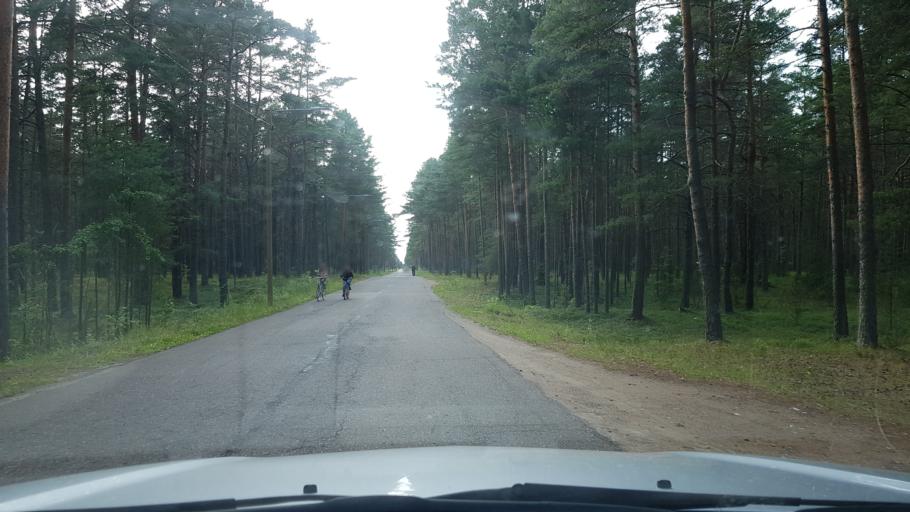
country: EE
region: Ida-Virumaa
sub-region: Narva-Joesuu linn
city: Narva-Joesuu
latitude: 59.4498
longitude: 28.0648
